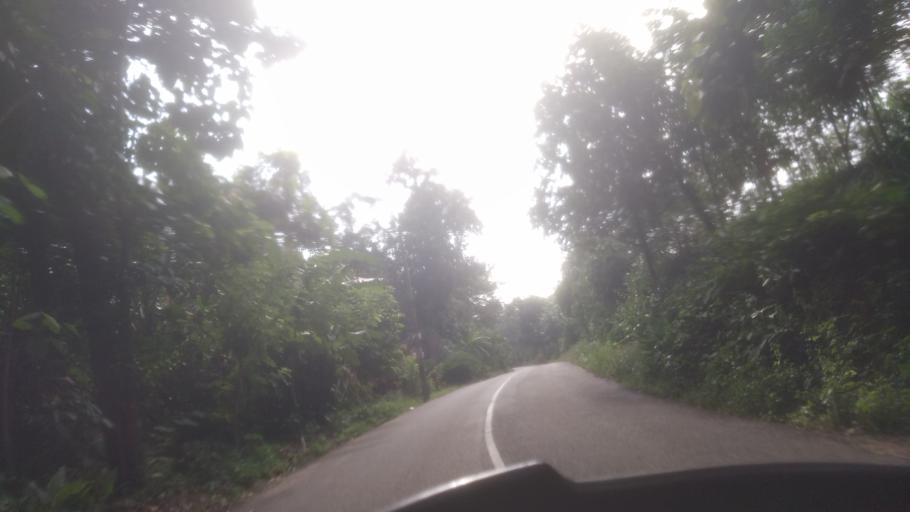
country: IN
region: Kerala
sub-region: Ernakulam
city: Kotamangalam
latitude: 9.9997
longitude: 76.6452
